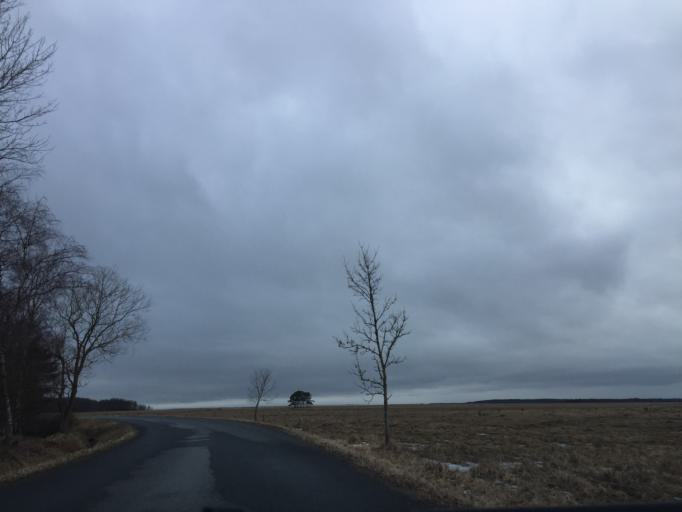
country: EE
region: Laeaene
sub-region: Haapsalu linn
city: Haapsalu
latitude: 58.8009
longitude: 23.5090
